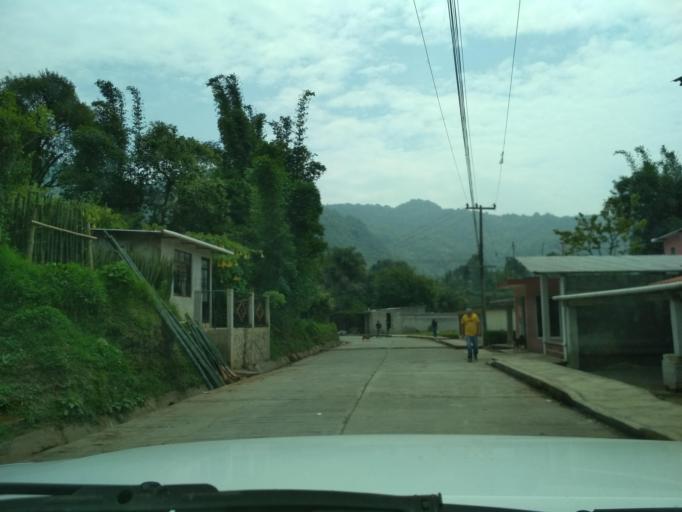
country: MX
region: Veracruz
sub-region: La Perla
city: Barrio de San Miguel
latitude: 18.9313
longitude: -97.1292
